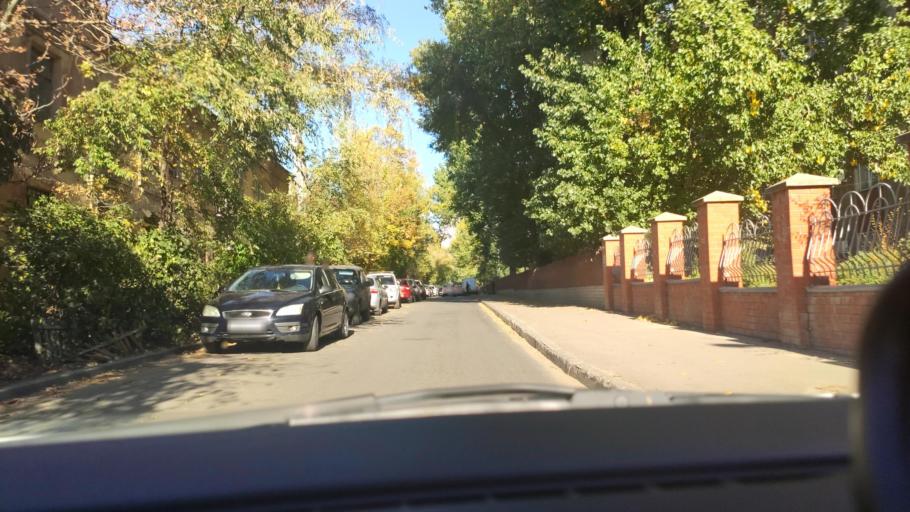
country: RU
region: Voronezj
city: Voronezh
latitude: 51.6947
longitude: 39.2041
